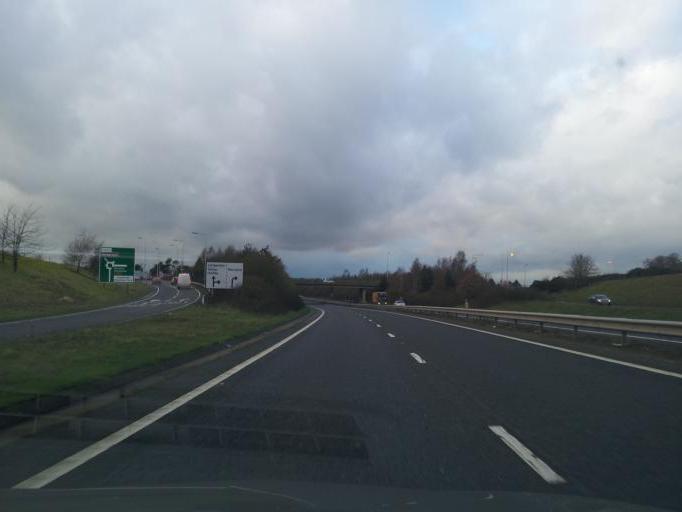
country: GB
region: England
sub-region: Norfolk
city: Costessey
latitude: 52.6488
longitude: 1.1872
